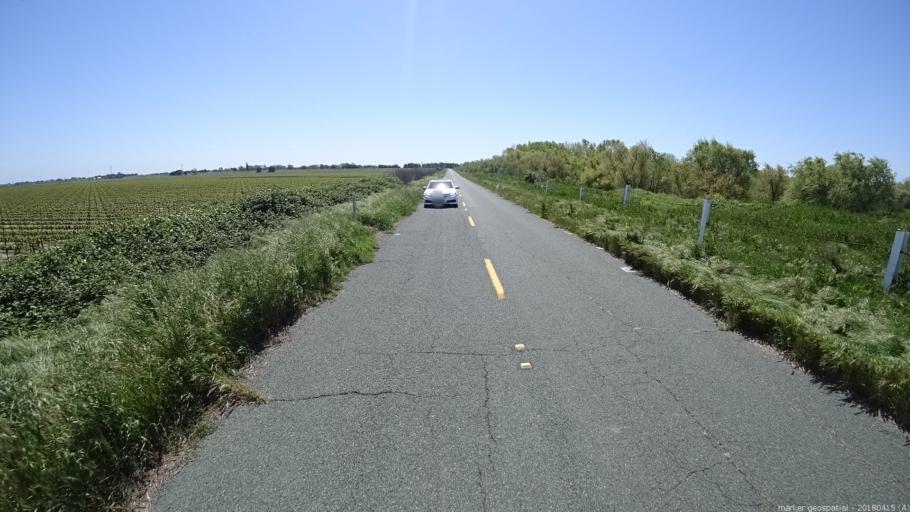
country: US
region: California
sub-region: Solano County
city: Rio Vista
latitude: 38.1821
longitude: -121.6480
